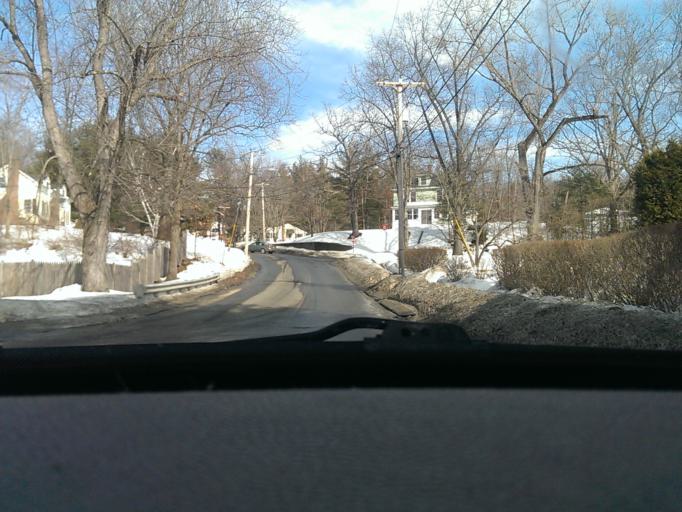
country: US
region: Massachusetts
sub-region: Hampden County
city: Palmer
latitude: 42.1642
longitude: -72.3412
